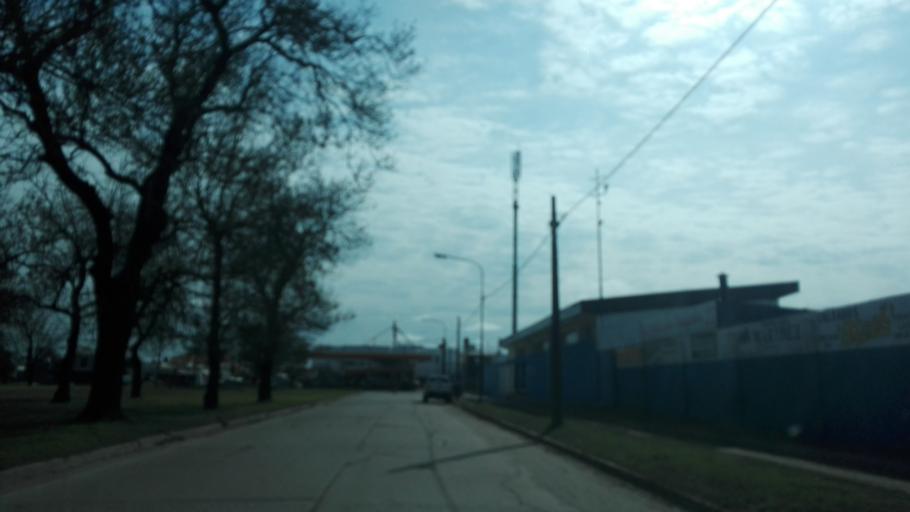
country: AR
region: Buenos Aires
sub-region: Partido de Chascomus
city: Chascomus
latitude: -35.5685
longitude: -58.0099
